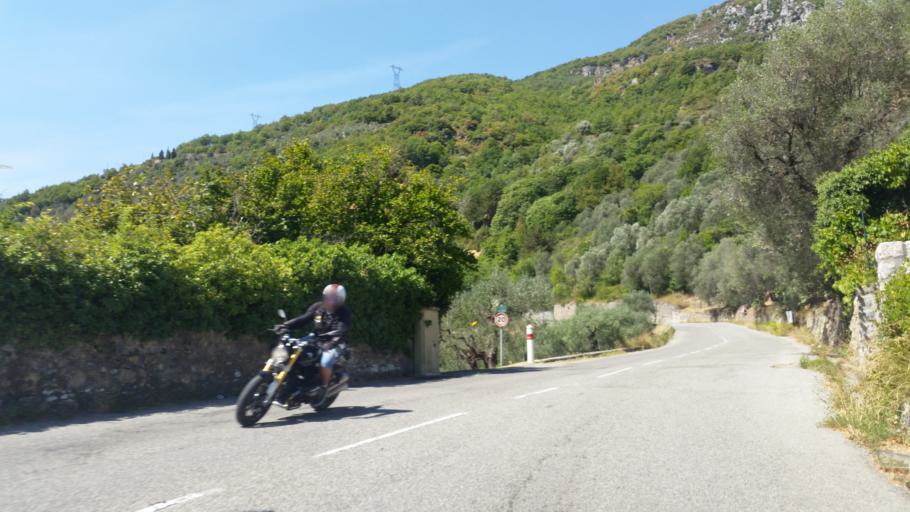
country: FR
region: Provence-Alpes-Cote d'Azur
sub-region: Departement des Alpes-Maritimes
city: Breil-sur-Roya
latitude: 43.9490
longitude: 7.5151
